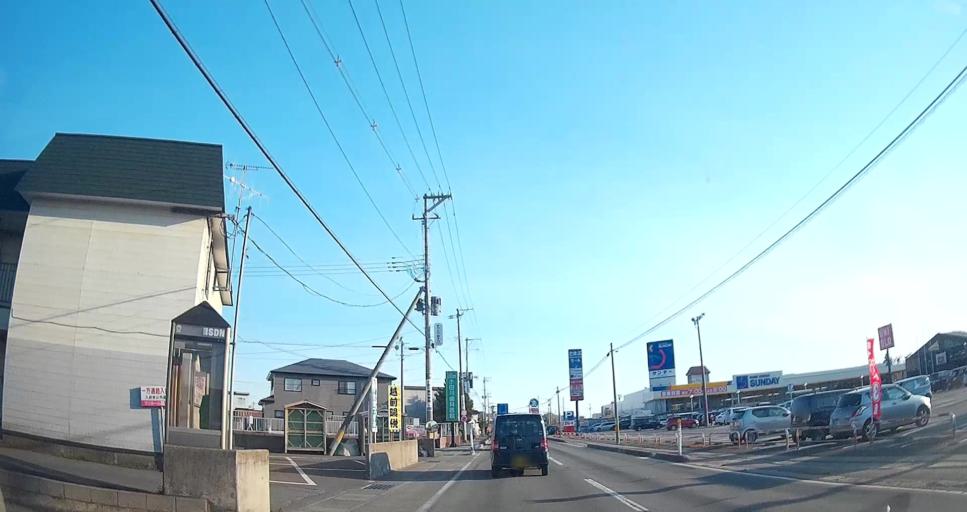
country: JP
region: Aomori
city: Mutsu
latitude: 41.2856
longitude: 141.2113
